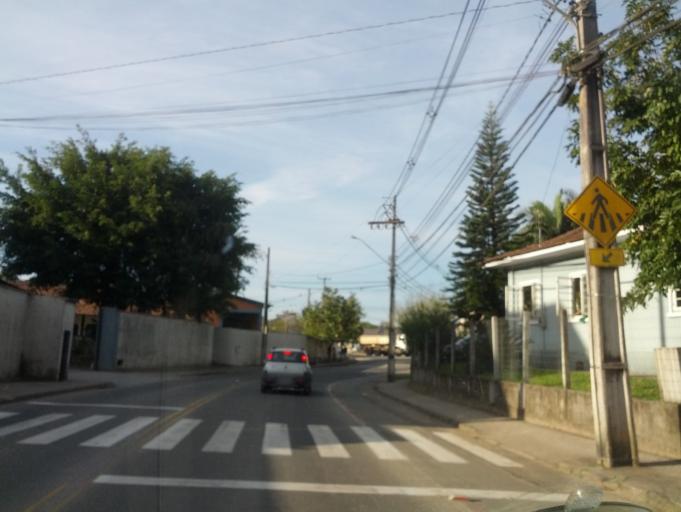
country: BR
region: Santa Catarina
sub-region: Indaial
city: Indaial
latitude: -26.9011
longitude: -49.1501
